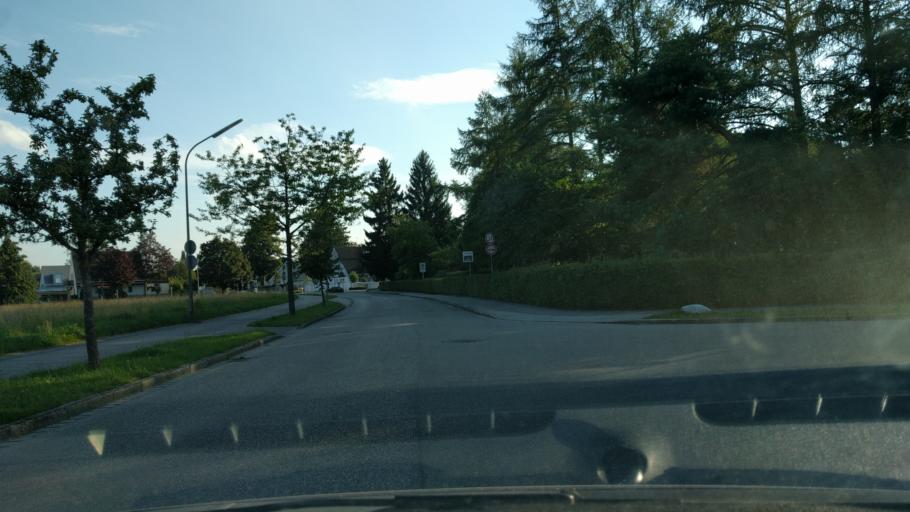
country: DE
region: Bavaria
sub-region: Upper Bavaria
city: Grunwald
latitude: 48.0418
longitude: 11.5362
